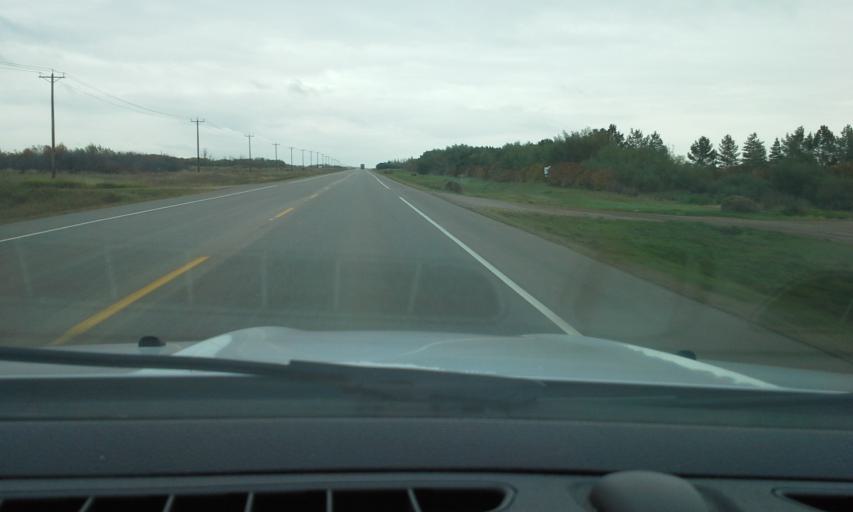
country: CA
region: Saskatchewan
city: Lloydminster
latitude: 53.2780
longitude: -109.8425
